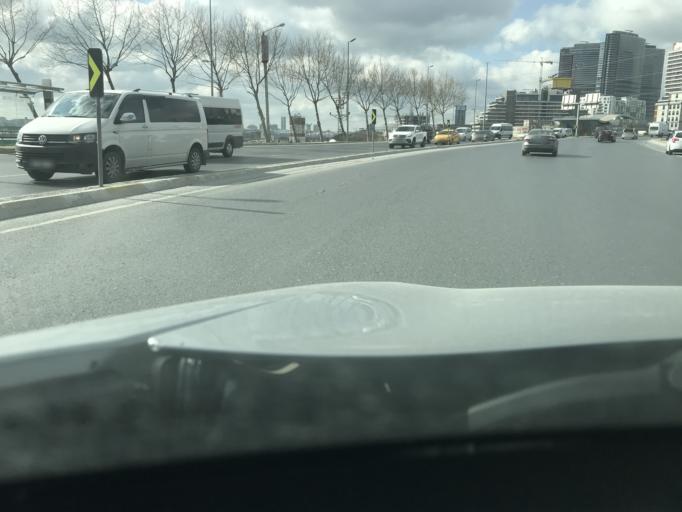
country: TR
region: Istanbul
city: Esenyurt
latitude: 41.0521
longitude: 28.6710
